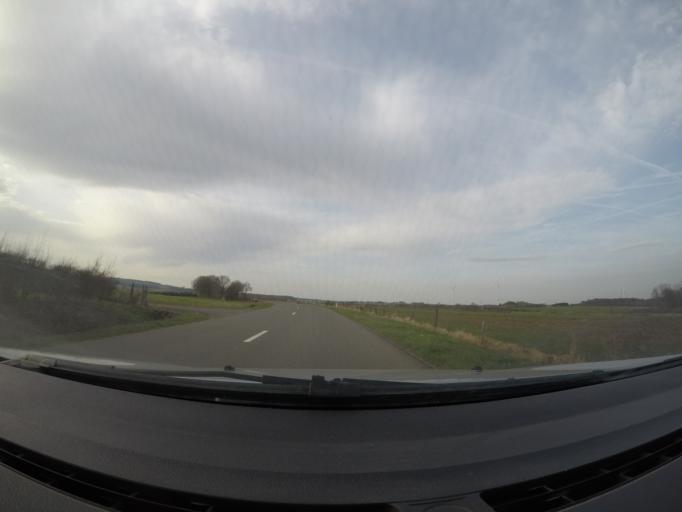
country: LU
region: Luxembourg
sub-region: Canton de Capellen
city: Clemency
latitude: 49.6226
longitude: 5.8451
